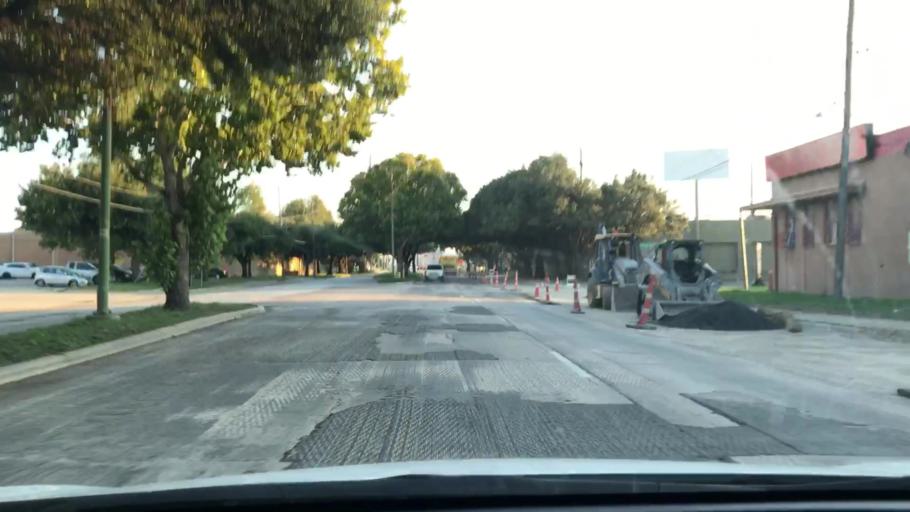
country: US
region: Texas
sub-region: Dallas County
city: Dallas
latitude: 32.7993
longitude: -96.8332
